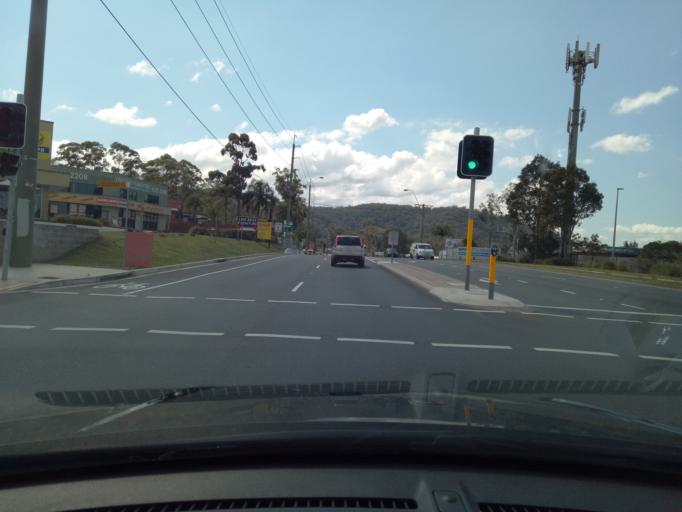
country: AU
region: New South Wales
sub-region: Gosford Shire
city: Point Clare
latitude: -33.4231
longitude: 151.3196
